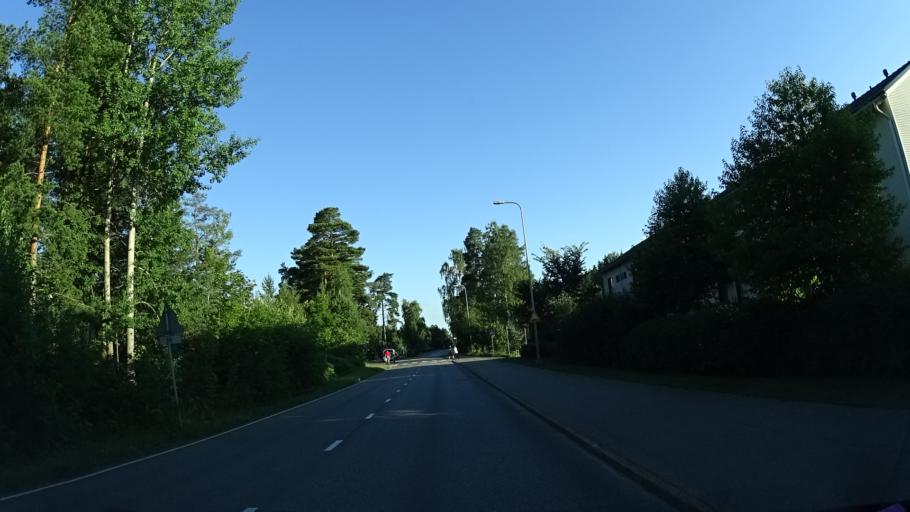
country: FI
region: Uusimaa
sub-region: Helsinki
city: Teekkarikylae
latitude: 60.2829
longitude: 24.8751
